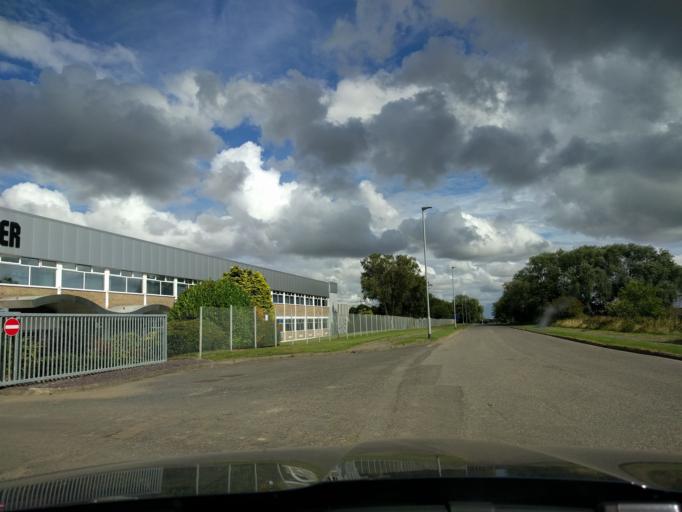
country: GB
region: England
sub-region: Northumberland
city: Cramlington
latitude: 55.0910
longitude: -1.6170
